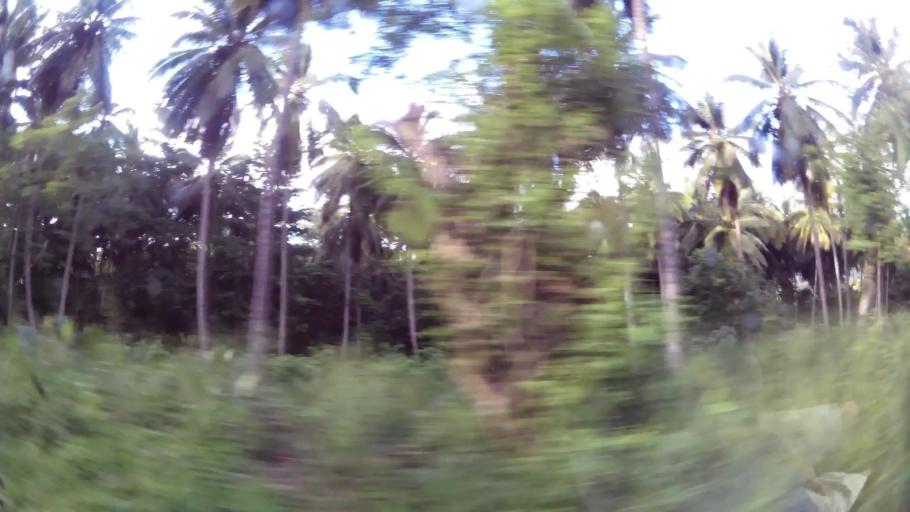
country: DM
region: Saint Joseph
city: Saint Joseph
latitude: 15.3938
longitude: -61.4232
